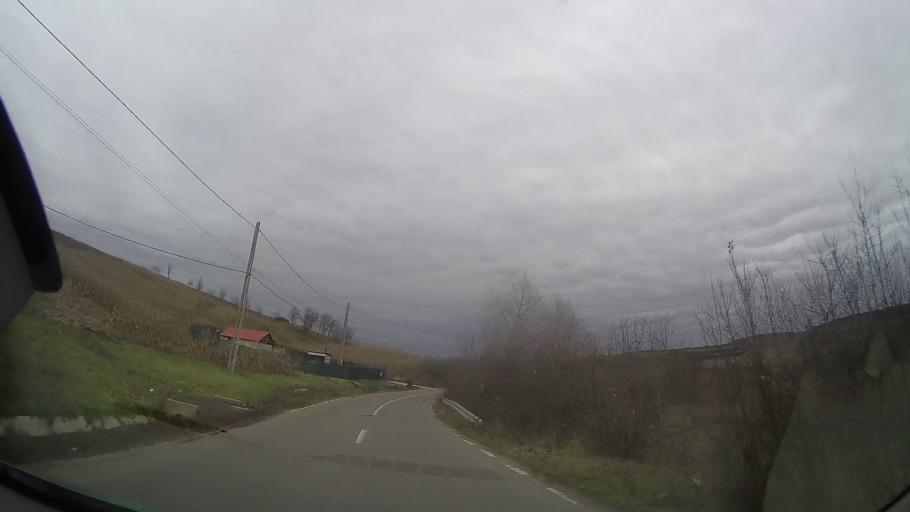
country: RO
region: Cluj
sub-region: Comuna Geaca
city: Geaca
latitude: 46.8362
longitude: 24.1340
